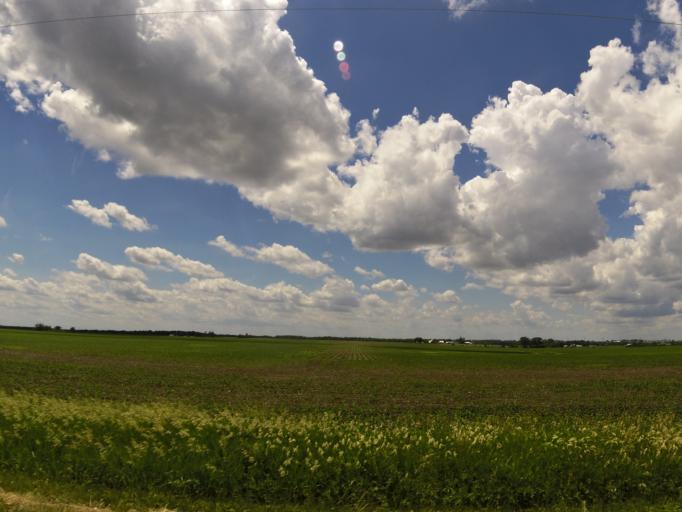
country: US
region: Iowa
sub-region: Buchanan County
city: Independence
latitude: 42.5627
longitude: -91.9049
